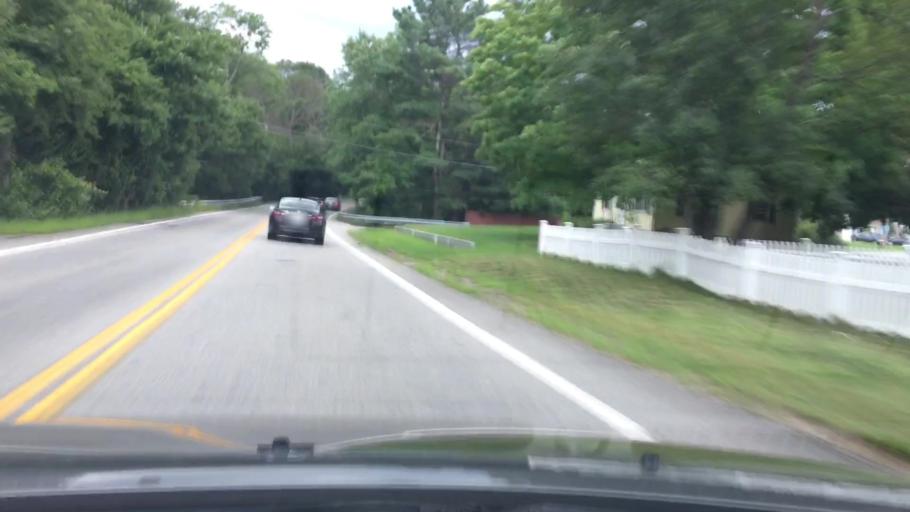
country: US
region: Rhode Island
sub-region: Providence County
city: Cumberland
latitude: 41.9969
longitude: -71.4171
